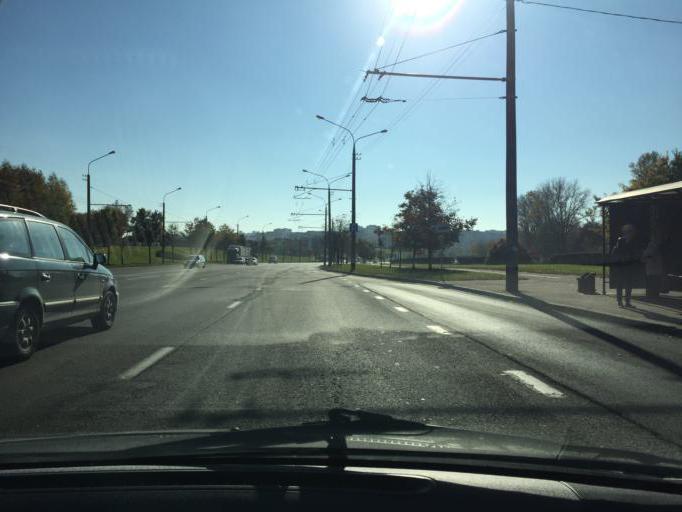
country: BY
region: Minsk
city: Syenitsa
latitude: 53.8618
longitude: 27.5350
